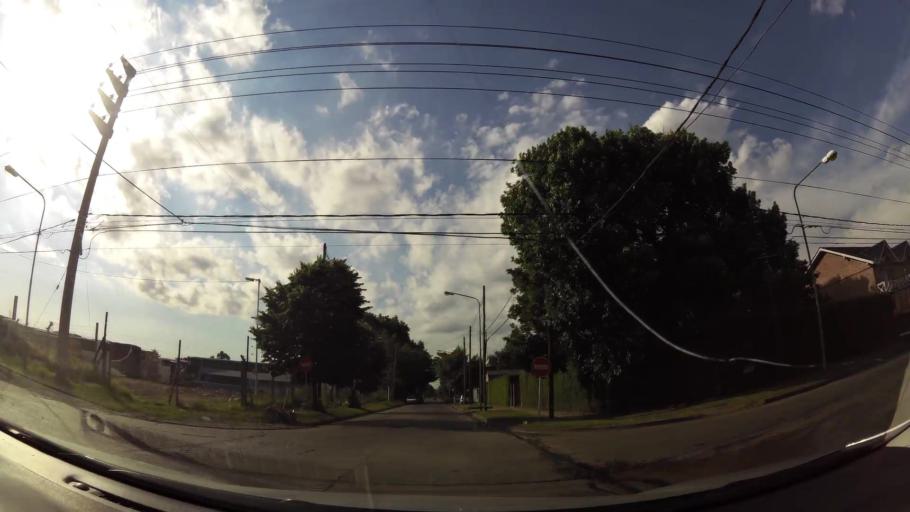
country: AR
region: Buenos Aires
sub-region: Partido de Tigre
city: Tigre
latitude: -34.4740
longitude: -58.6543
